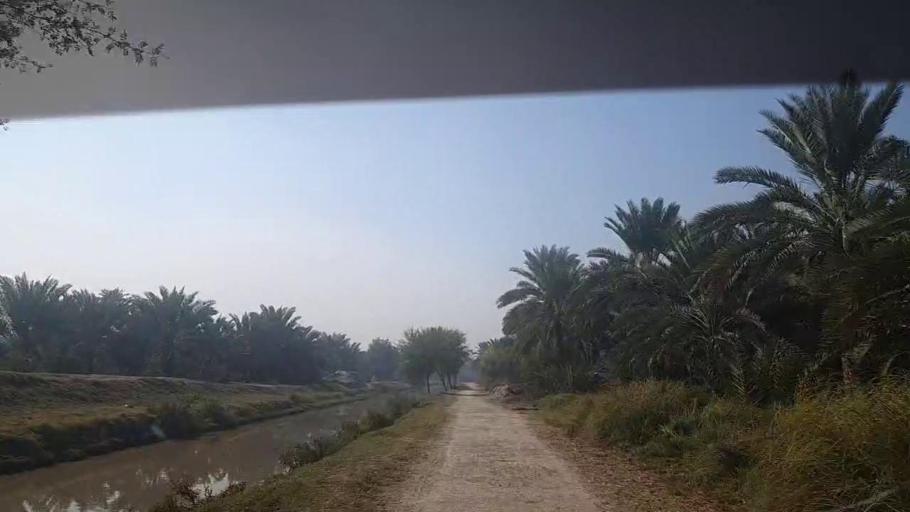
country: PK
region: Sindh
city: Khairpur
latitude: 27.4733
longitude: 68.7267
